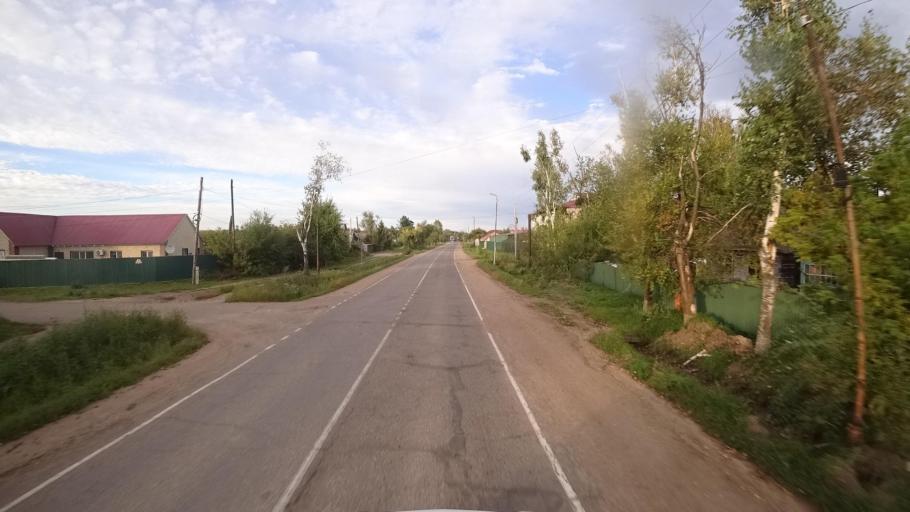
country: RU
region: Primorskiy
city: Yakovlevka
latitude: 44.4285
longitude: 133.4815
